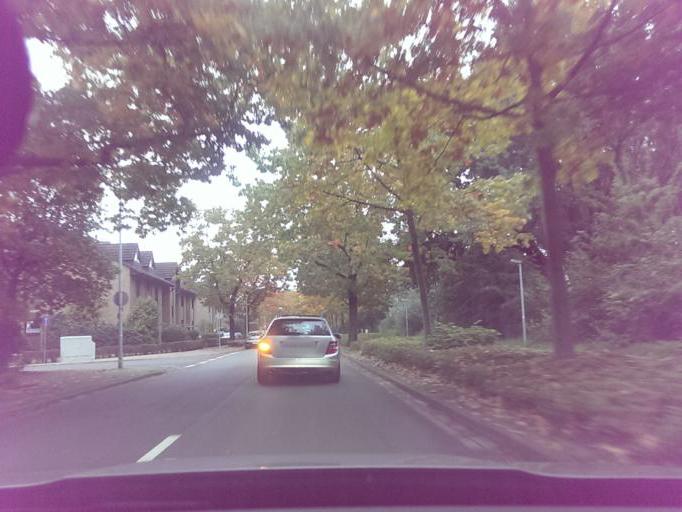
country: DE
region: Lower Saxony
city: Garbsen-Mitte
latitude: 52.4310
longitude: 9.5956
